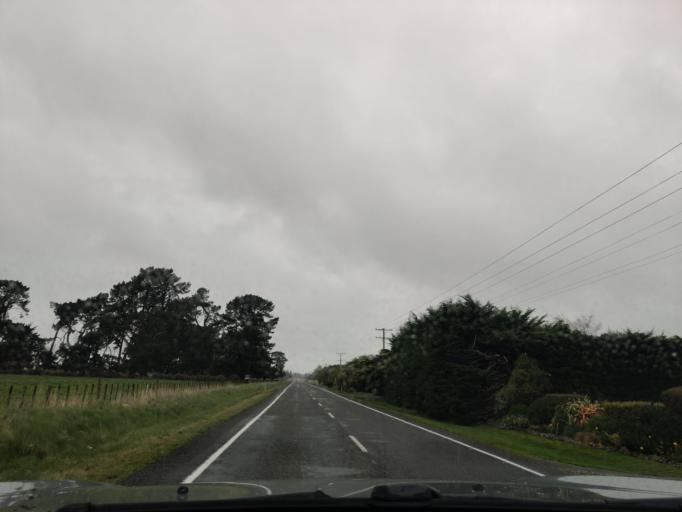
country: NZ
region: Hawke's Bay
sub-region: Hastings District
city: Hastings
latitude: -40.0189
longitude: 176.3449
